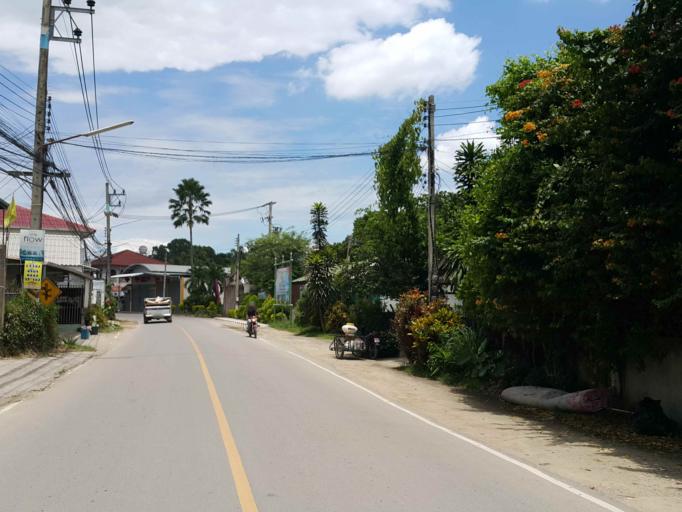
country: TH
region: Chiang Mai
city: San Sai
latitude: 18.8638
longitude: 98.9834
